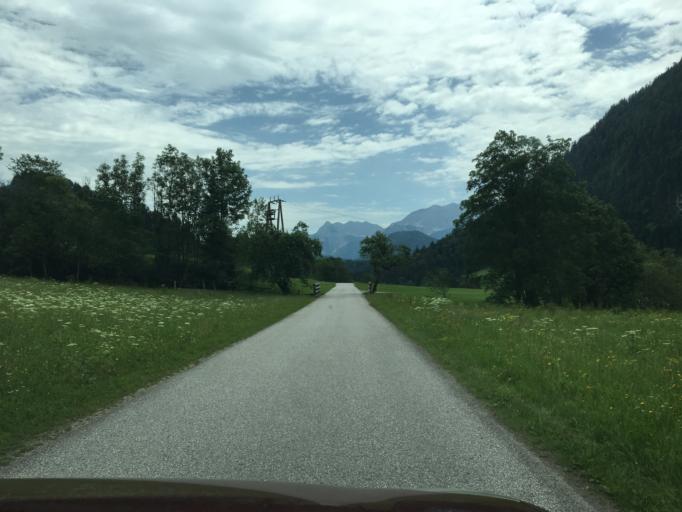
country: AT
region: Salzburg
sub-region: Politischer Bezirk Hallein
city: Scheffau am Tennengebirge
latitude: 47.6174
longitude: 13.2538
